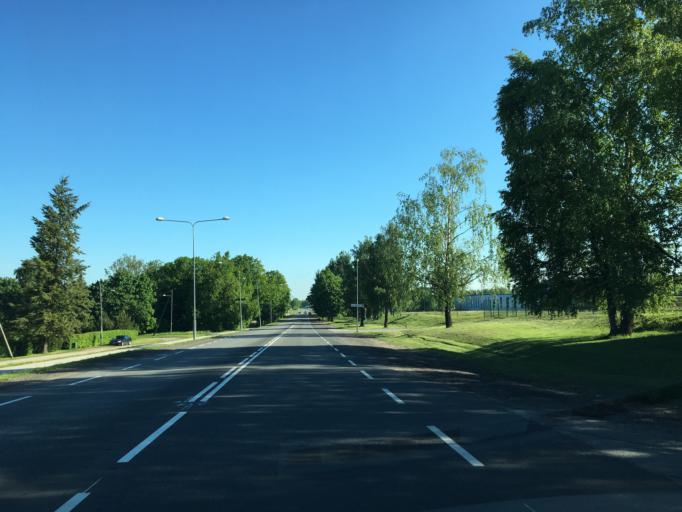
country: EE
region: Tartu
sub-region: Tartu linn
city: Tartu
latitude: 58.4004
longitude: 26.7084
